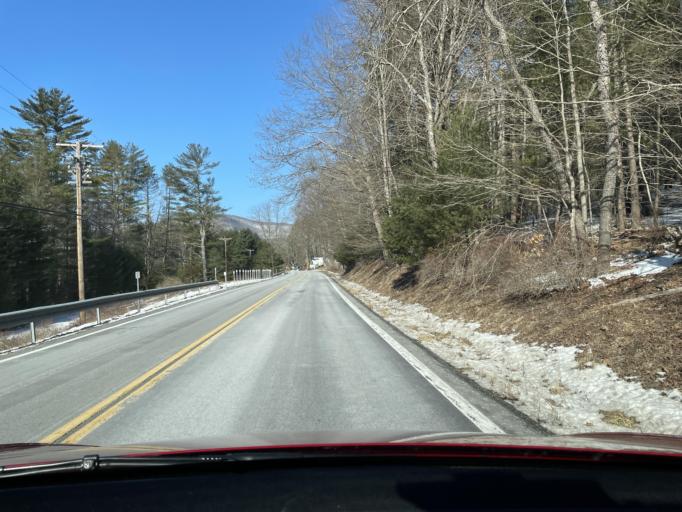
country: US
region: New York
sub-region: Ulster County
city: Woodstock
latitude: 42.0768
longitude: -74.2083
